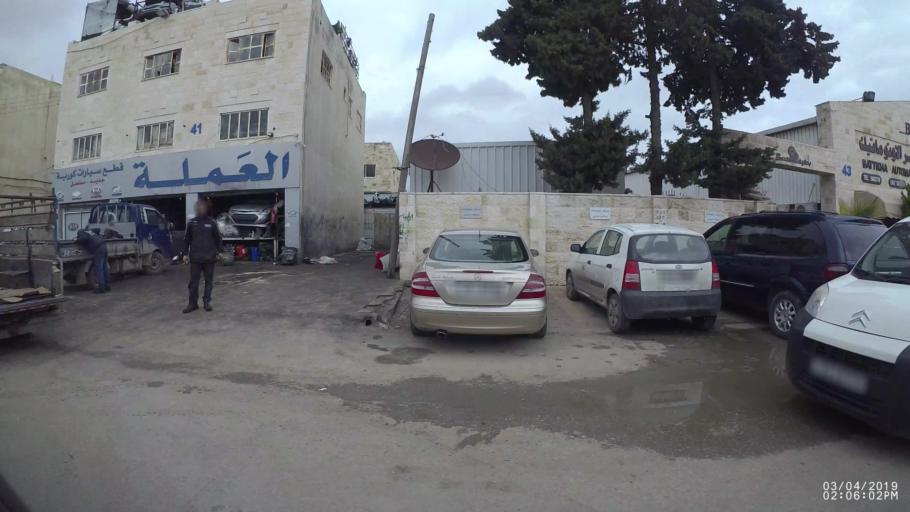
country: JO
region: Amman
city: Wadi as Sir
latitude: 31.9418
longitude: 35.8435
